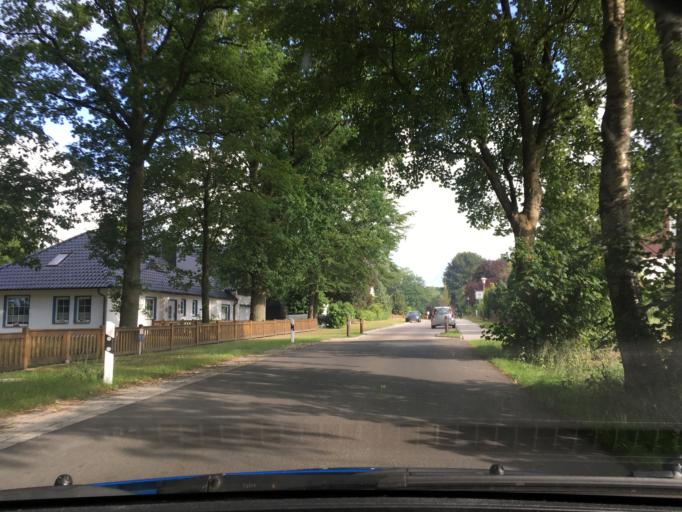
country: DE
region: Lower Saxony
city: Kakenstorf
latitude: 53.3099
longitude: 9.7750
